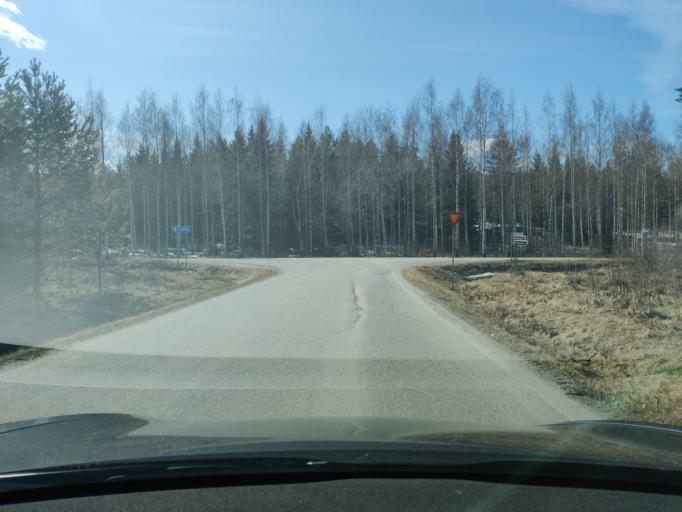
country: FI
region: Northern Savo
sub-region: Kuopio
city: Vehmersalmi
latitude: 62.7719
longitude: 27.9783
